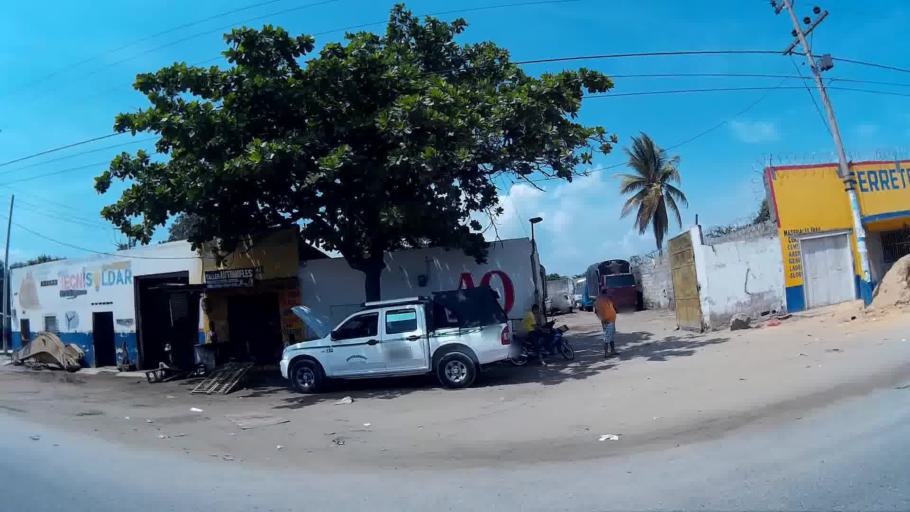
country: CO
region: Magdalena
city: Cienaga
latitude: 11.0055
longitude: -74.2425
